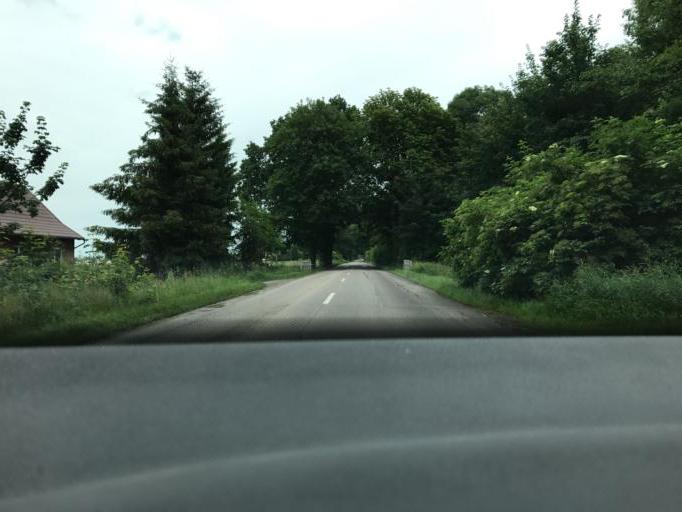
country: PL
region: Pomeranian Voivodeship
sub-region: Powiat gdanski
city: Suchy Dab
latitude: 54.2463
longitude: 18.7283
